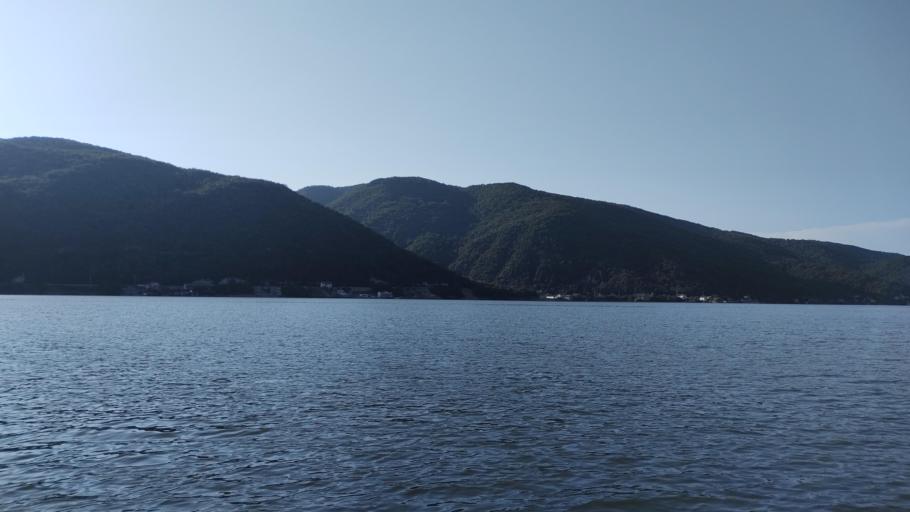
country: RO
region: Mehedinti
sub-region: Comuna Dubova
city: Dubova
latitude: 44.5629
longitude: 22.2350
